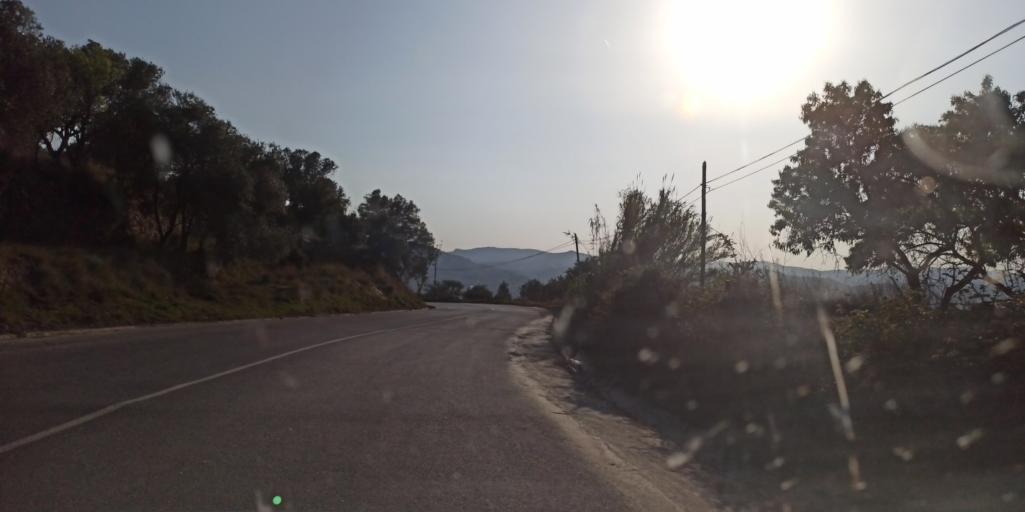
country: ES
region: Catalonia
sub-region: Provincia de Barcelona
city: Sant Feliu de Llobregat
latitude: 41.3970
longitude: 2.0532
